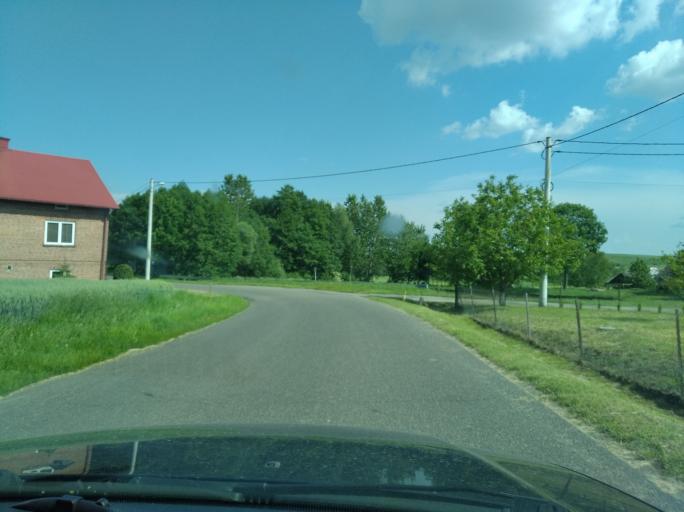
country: PL
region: Subcarpathian Voivodeship
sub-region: Powiat jaroslawski
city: Rokietnica
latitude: 49.9418
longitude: 22.7006
